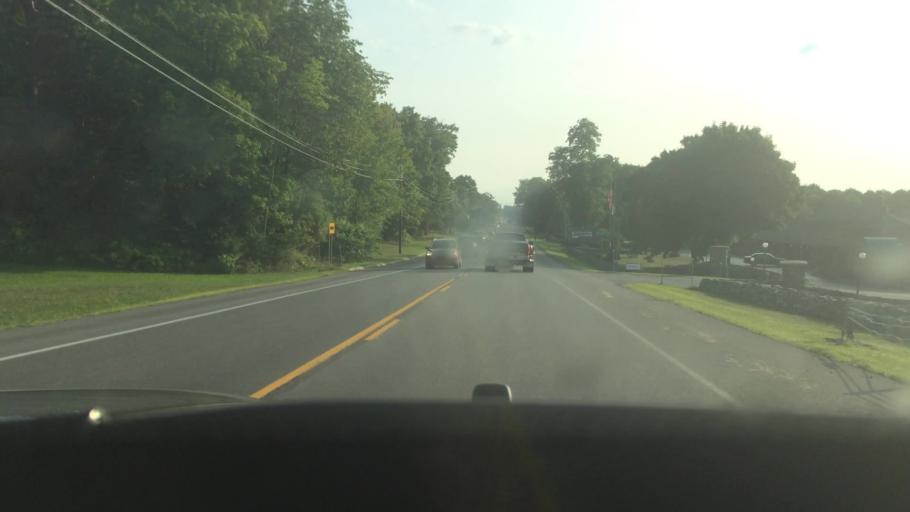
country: CA
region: Ontario
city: Prescott
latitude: 44.6743
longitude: -75.5269
